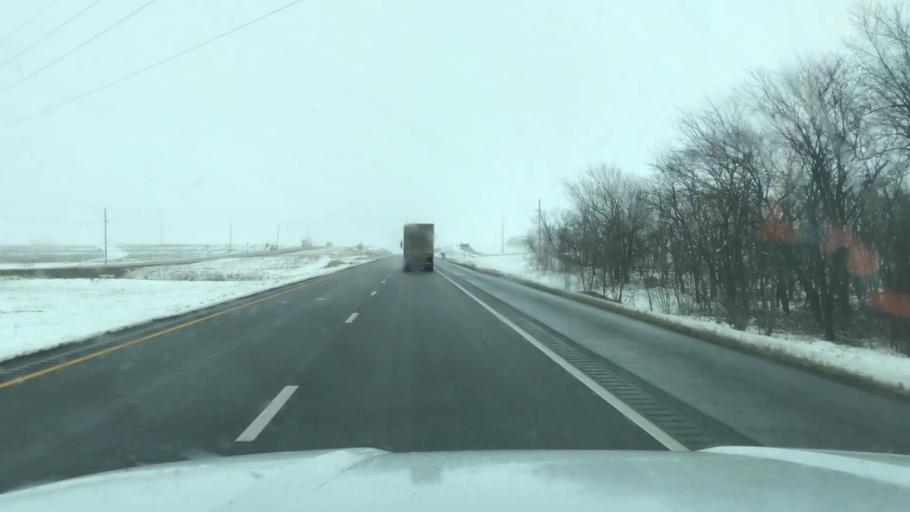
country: US
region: Missouri
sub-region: DeKalb County
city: Maysville
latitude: 39.7619
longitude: -94.4536
